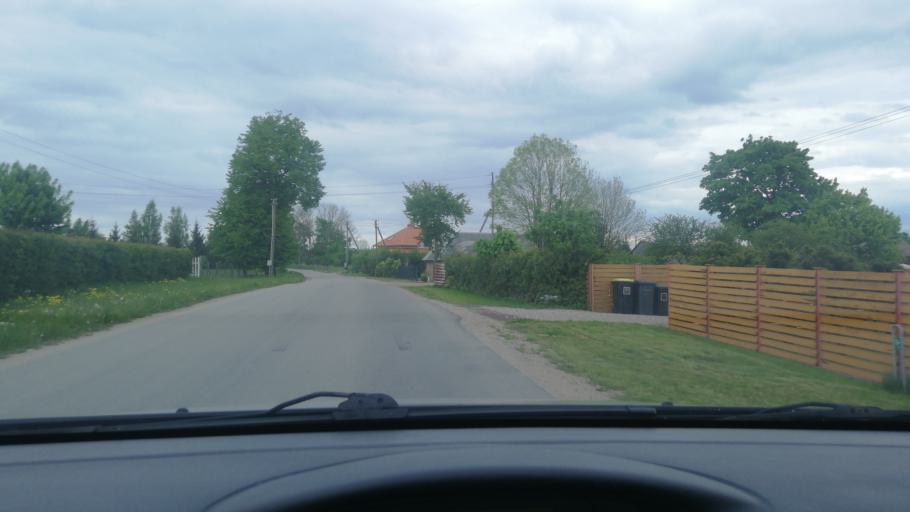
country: LT
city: Priekule
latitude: 55.6448
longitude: 21.2969
